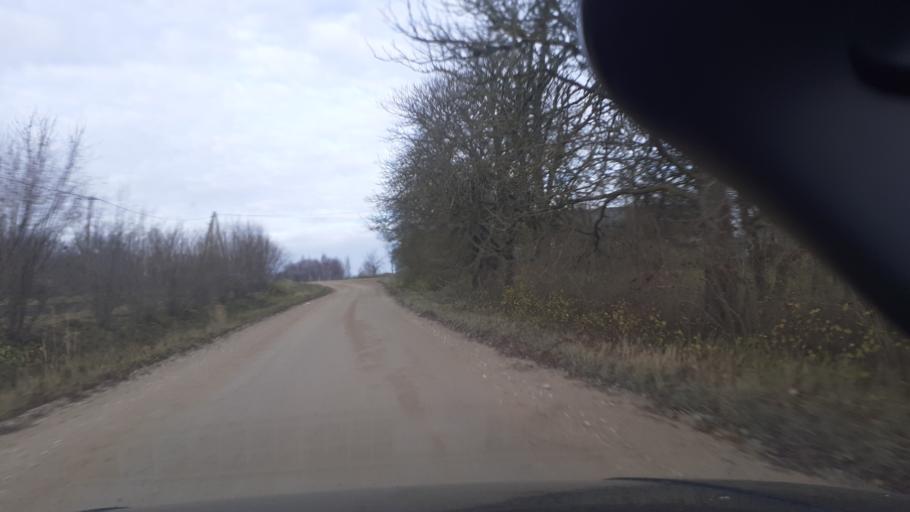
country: LV
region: Alsunga
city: Alsunga
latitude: 56.9118
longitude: 21.6567
